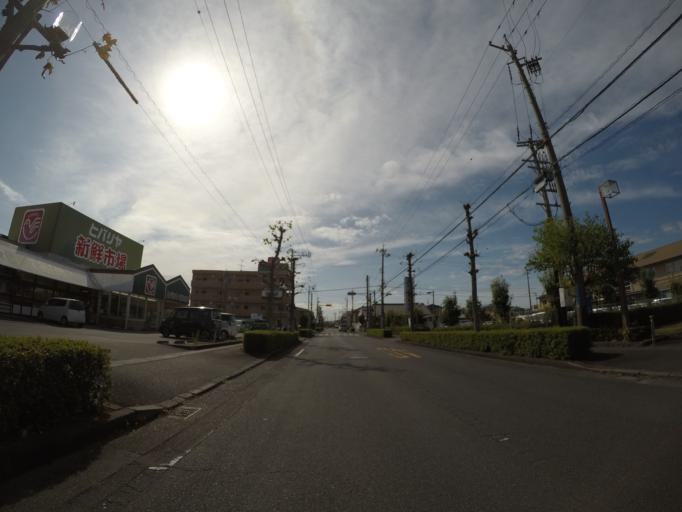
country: JP
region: Shizuoka
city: Yaizu
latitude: 34.8574
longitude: 138.3069
